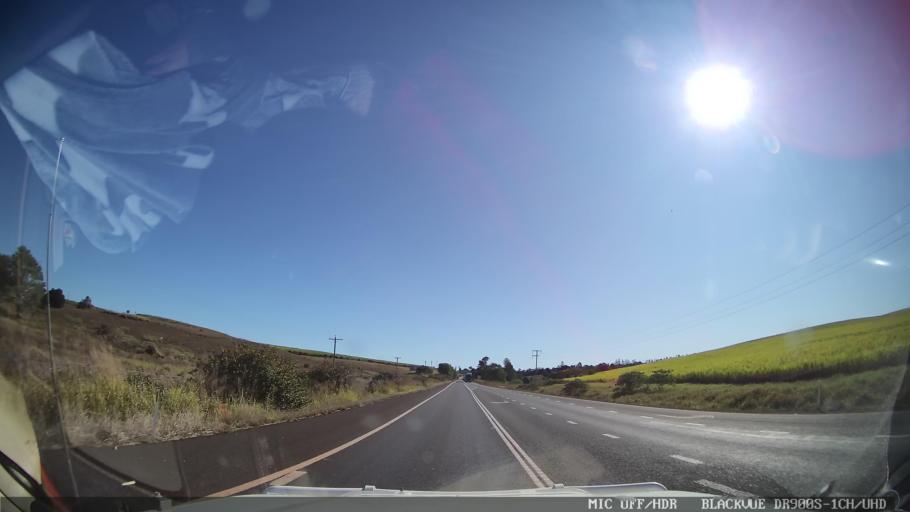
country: AU
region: Queensland
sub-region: Bundaberg
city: Childers
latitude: -25.2449
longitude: 152.3090
